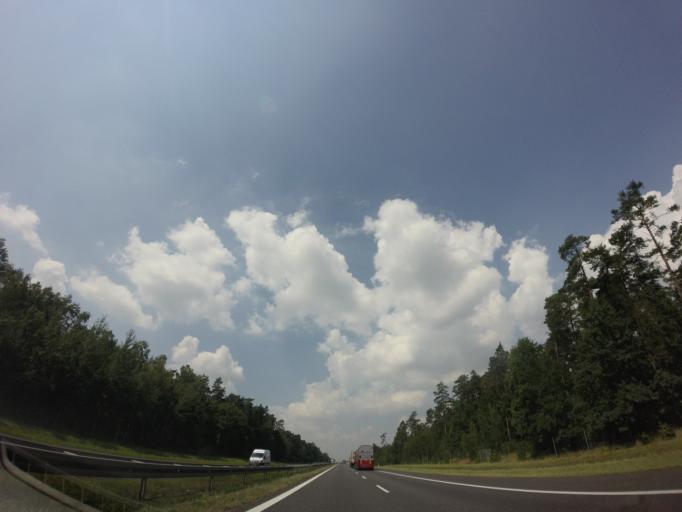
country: PL
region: Silesian Voivodeship
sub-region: Powiat gliwicki
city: Toszek
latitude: 50.3689
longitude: 18.4973
